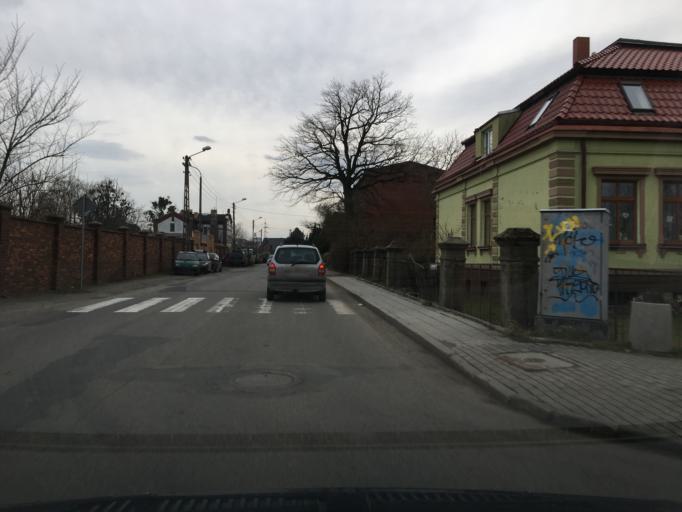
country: PL
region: Opole Voivodeship
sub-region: Powiat kedzierzynsko-kozielski
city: Kozle
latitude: 50.3480
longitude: 18.1426
